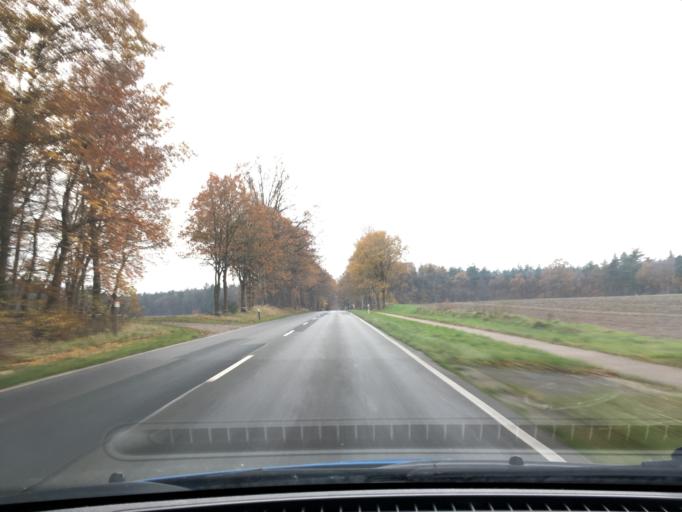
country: DE
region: Lower Saxony
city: Embsen
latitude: 53.2041
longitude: 10.3598
